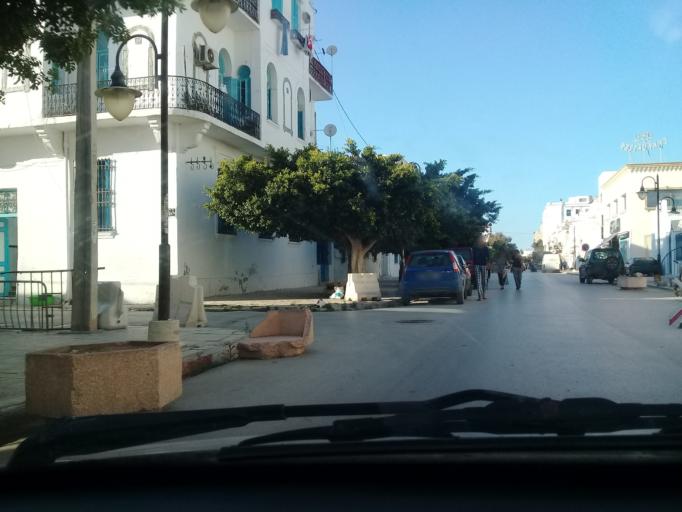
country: TN
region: Tunis
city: La Goulette
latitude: 36.8208
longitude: 10.3094
